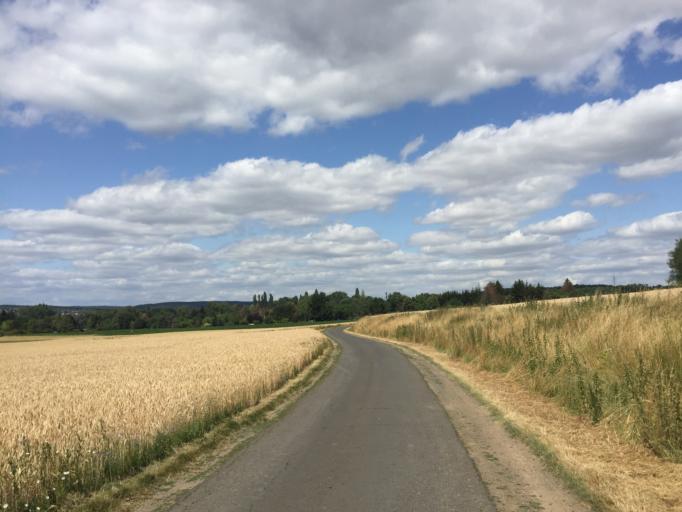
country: DE
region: Hesse
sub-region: Regierungsbezirk Giessen
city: Giessen
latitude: 50.6151
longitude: 8.6920
